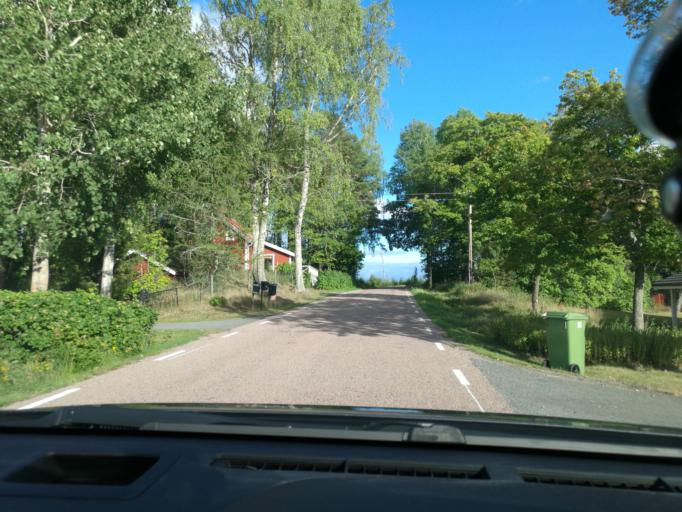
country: SE
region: Vaestmanland
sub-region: Kungsors Kommun
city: Kungsoer
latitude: 59.5470
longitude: 16.1174
